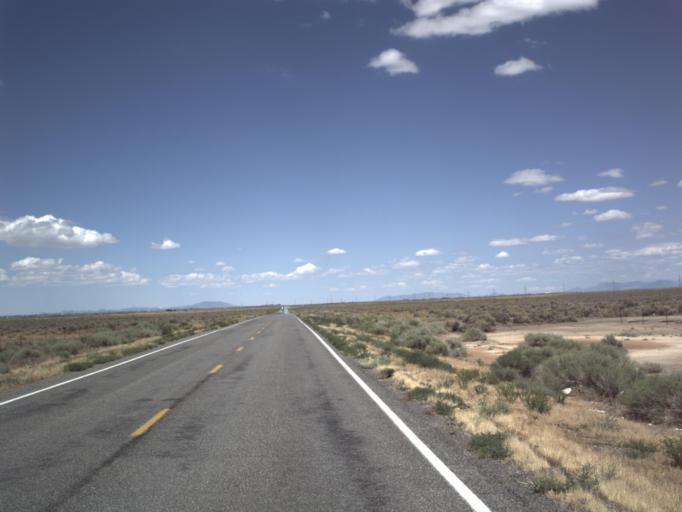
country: US
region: Utah
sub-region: Millard County
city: Delta
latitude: 39.2731
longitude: -112.4556
